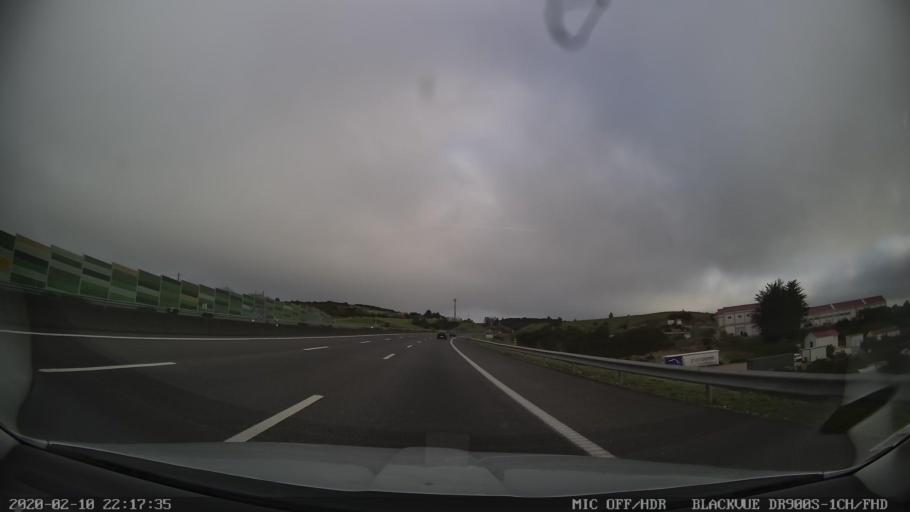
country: PT
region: Lisbon
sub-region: Loures
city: Bucelas
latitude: 38.9203
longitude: -9.0745
